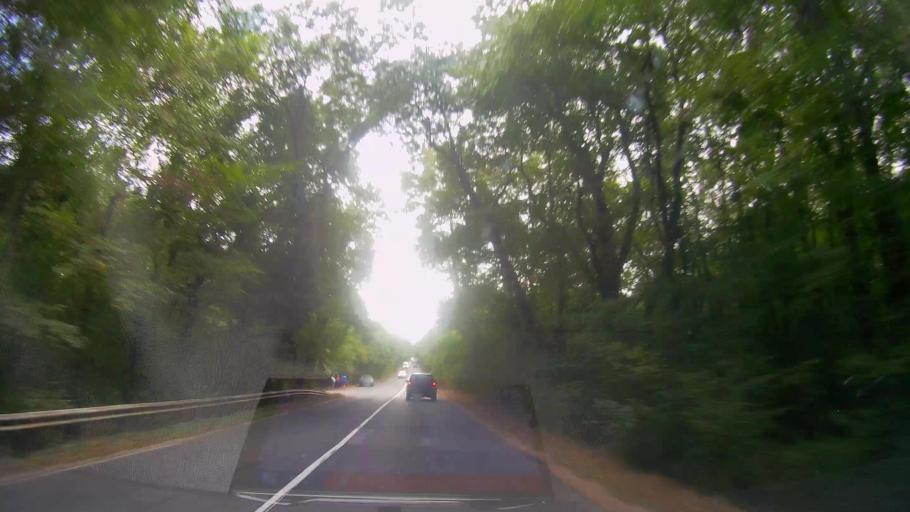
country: BG
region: Burgas
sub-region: Obshtina Primorsko
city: Primorsko
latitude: 42.3011
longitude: 27.7293
